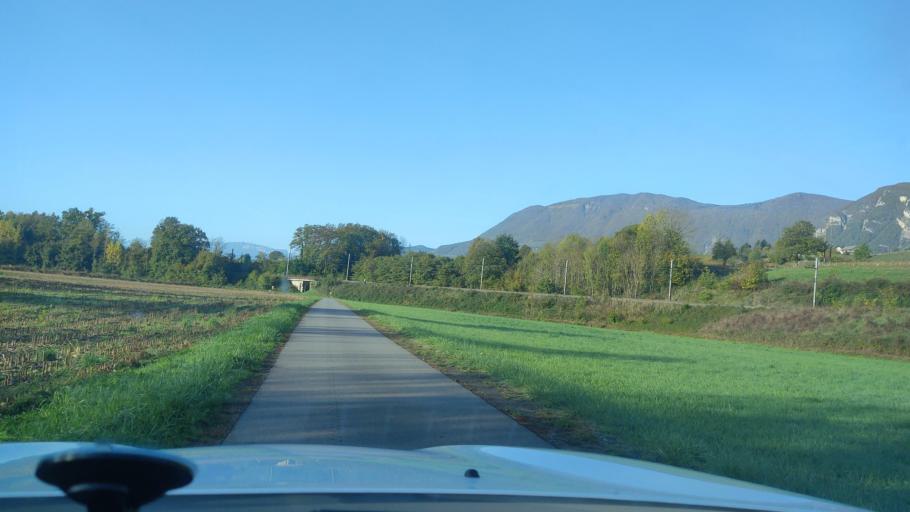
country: FR
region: Rhone-Alpes
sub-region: Departement de la Savoie
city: Coise-Saint-Jean-Pied-Gauthier
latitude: 45.5696
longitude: 6.1820
